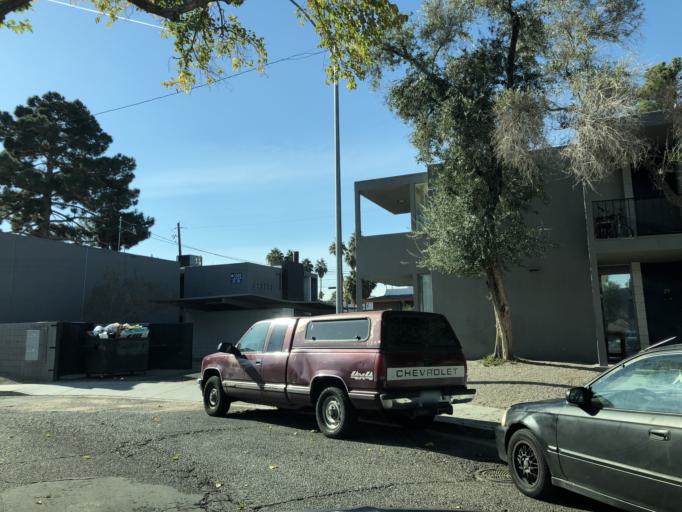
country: US
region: Nevada
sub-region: Clark County
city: Winchester
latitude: 36.1263
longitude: -115.1386
